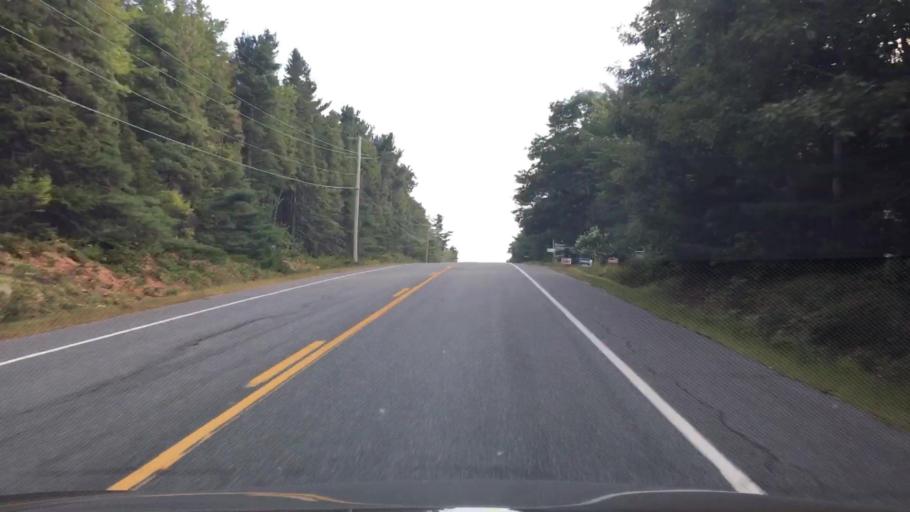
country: US
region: Maine
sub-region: Hancock County
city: Surry
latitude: 44.4802
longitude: -68.5185
